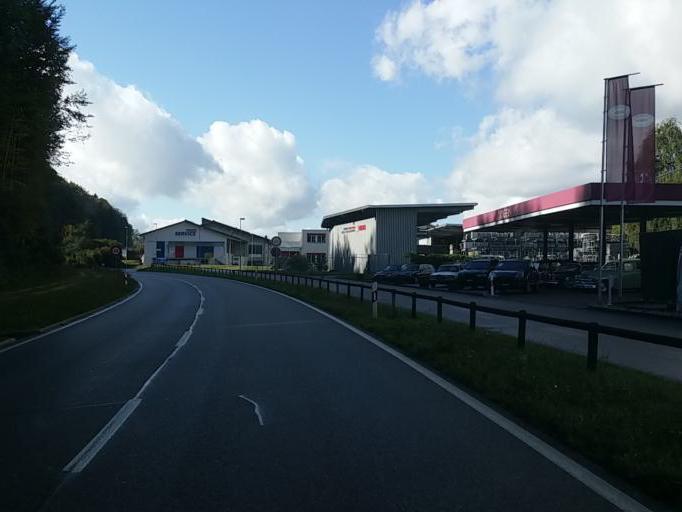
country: CH
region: Bern
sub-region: Oberaargau
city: Wangen an der Aare
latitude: 47.2316
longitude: 7.6585
